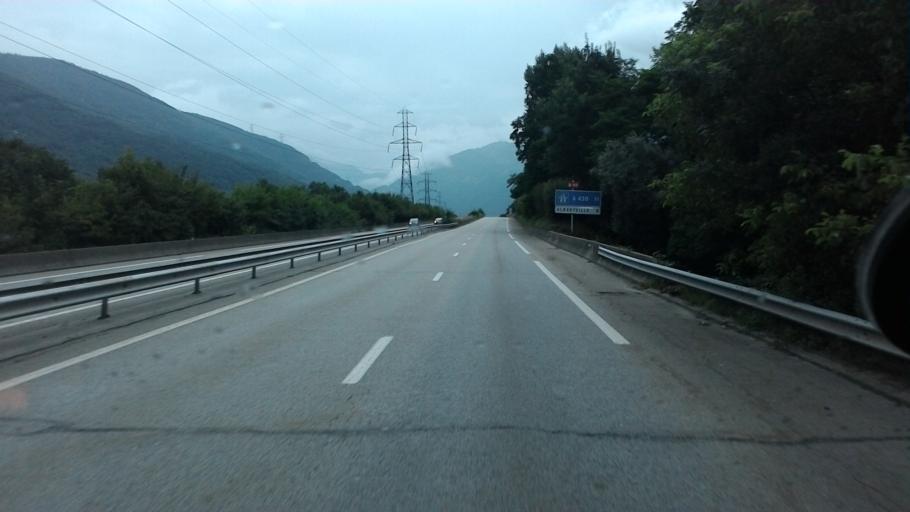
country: FR
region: Rhone-Alpes
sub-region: Departement de la Savoie
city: La Bathie
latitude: 45.6144
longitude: 6.4500
